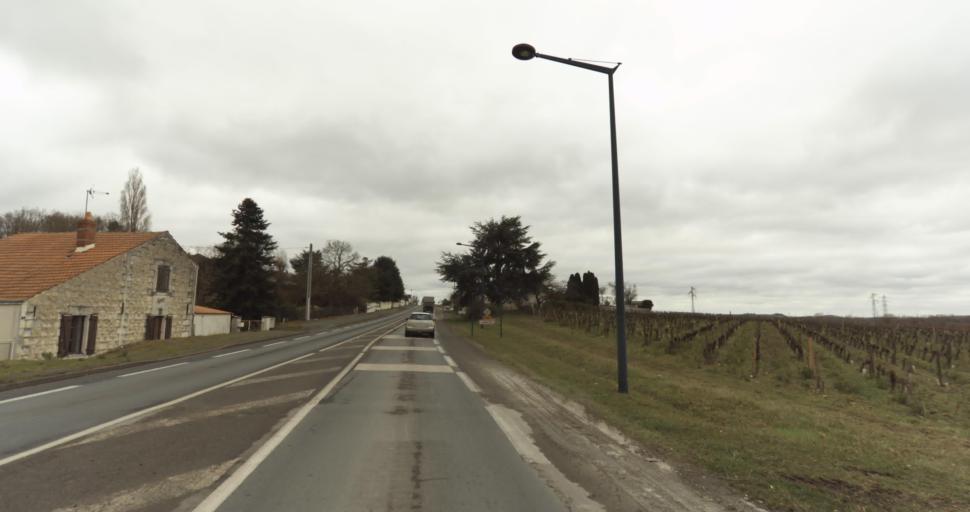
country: FR
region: Pays de la Loire
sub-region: Departement de Maine-et-Loire
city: Varrains
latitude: 47.2330
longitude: -0.0738
